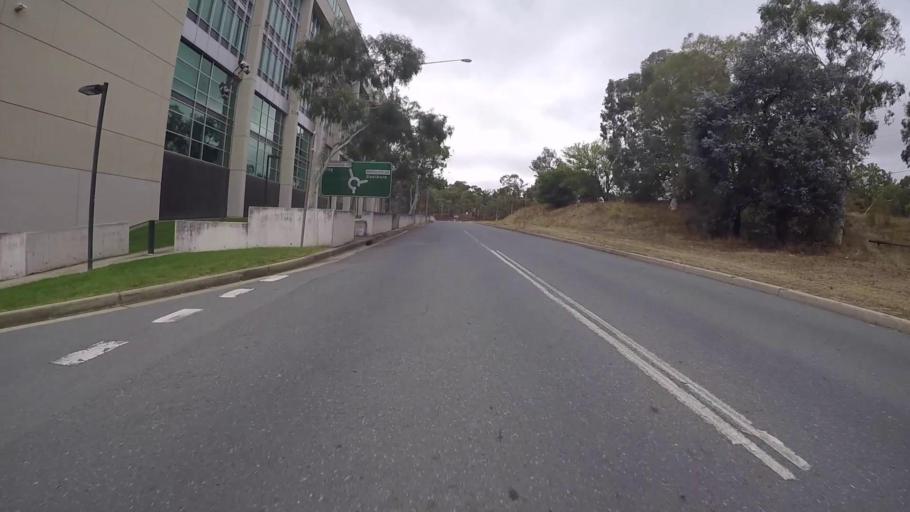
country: AU
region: Australian Capital Territory
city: Canberra
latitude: -35.2982
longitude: 149.1528
